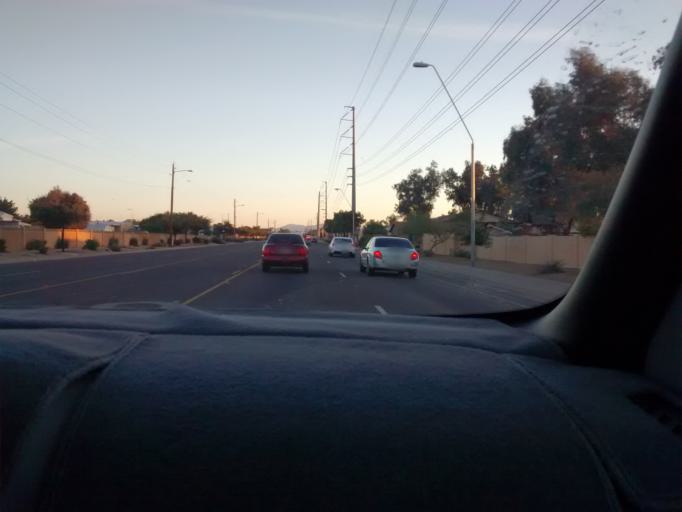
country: US
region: Arizona
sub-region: Maricopa County
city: Peoria
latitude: 33.5719
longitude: -112.2030
